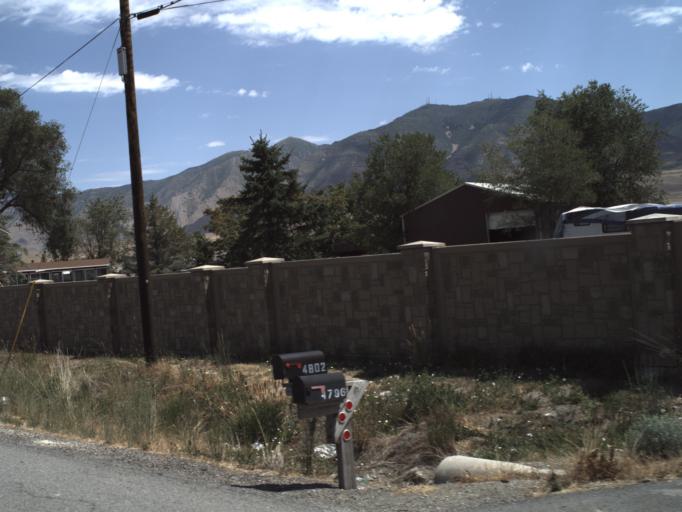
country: US
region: Utah
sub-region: Tooele County
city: Erda
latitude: 40.6135
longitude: -112.2946
